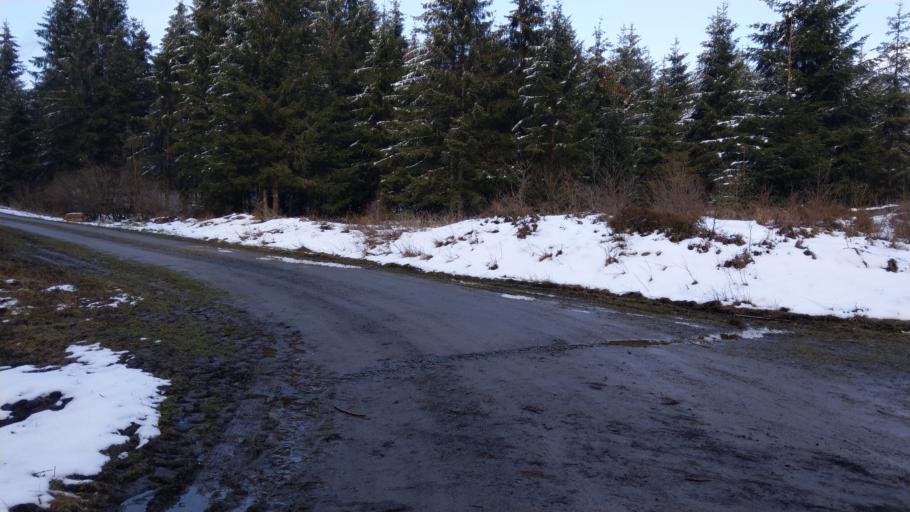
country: DE
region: North Rhine-Westphalia
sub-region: Regierungsbezirk Koln
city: Monschau
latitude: 50.5751
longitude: 6.1953
